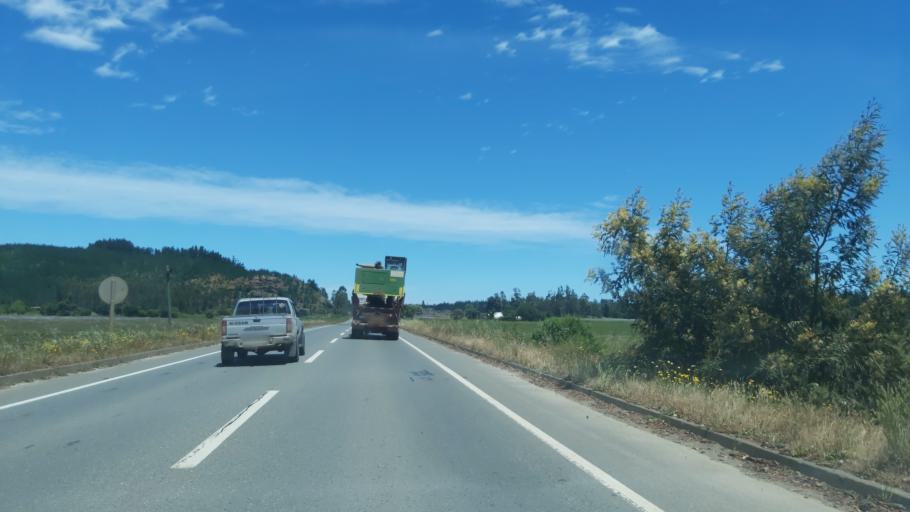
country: CL
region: Maule
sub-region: Provincia de Talca
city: Constitucion
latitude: -35.2774
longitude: -72.3508
